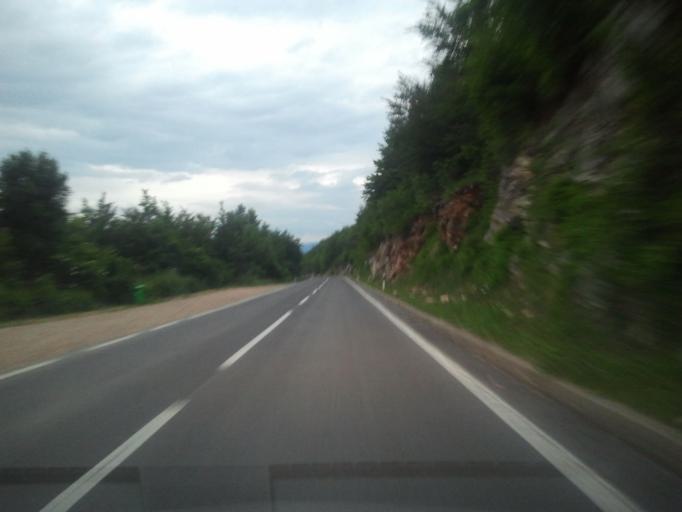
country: HR
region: Zadarska
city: Gracac
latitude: 44.2742
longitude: 15.8174
